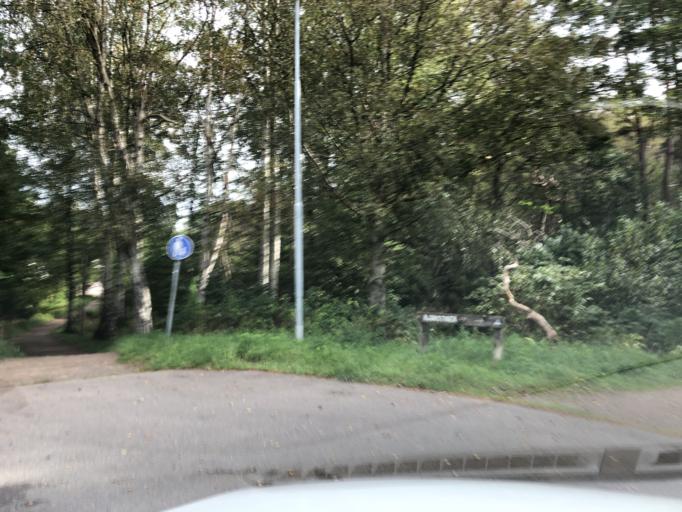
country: SE
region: Vaestra Goetaland
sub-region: Goteborg
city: Majorna
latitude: 57.7413
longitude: 11.9188
